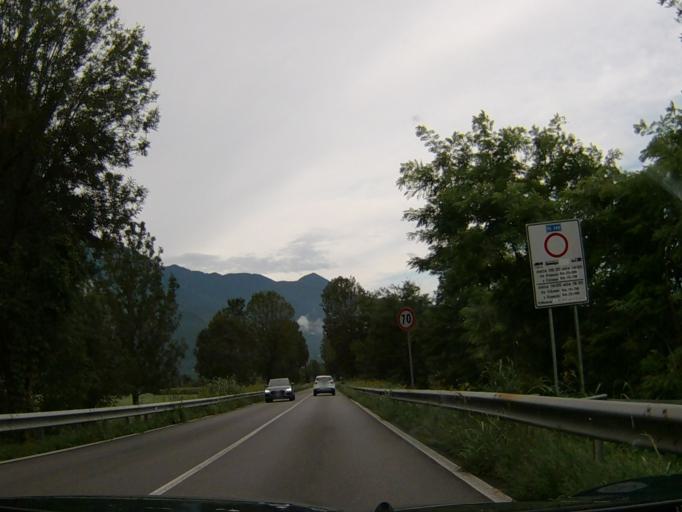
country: IT
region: Lombardy
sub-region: Provincia di Sondrio
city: Dubino
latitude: 46.1608
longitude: 9.4223
